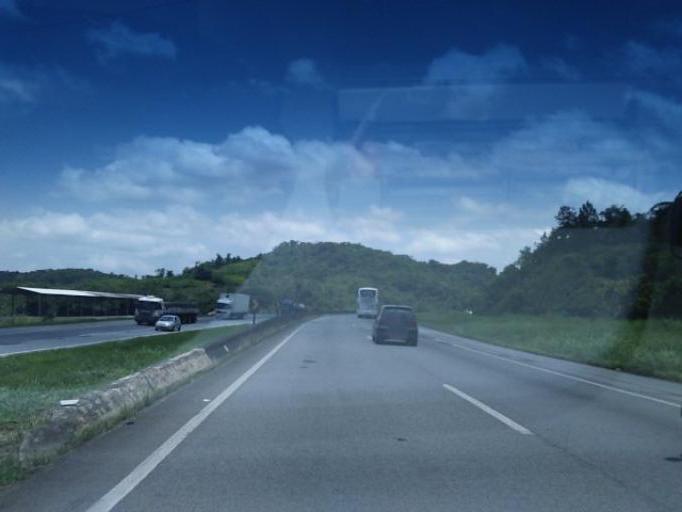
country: BR
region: Sao Paulo
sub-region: Juquia
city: Juquia
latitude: -24.3749
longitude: -47.7078
